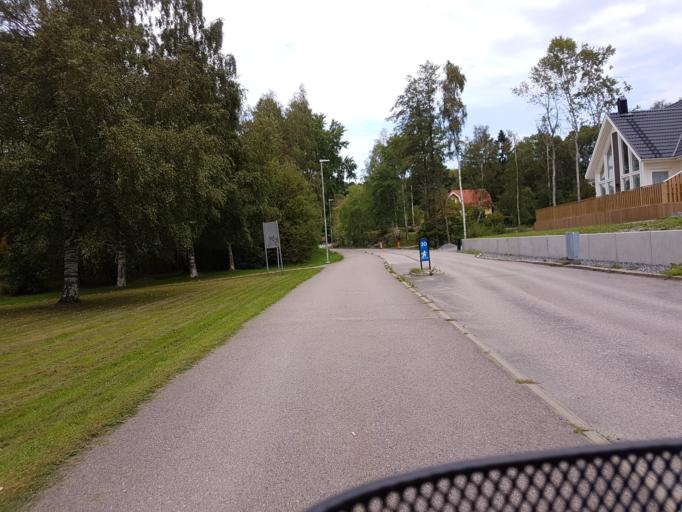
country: SE
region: Vaestra Goetaland
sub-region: Ale Kommun
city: Nodinge-Nol
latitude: 57.8976
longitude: 12.0568
